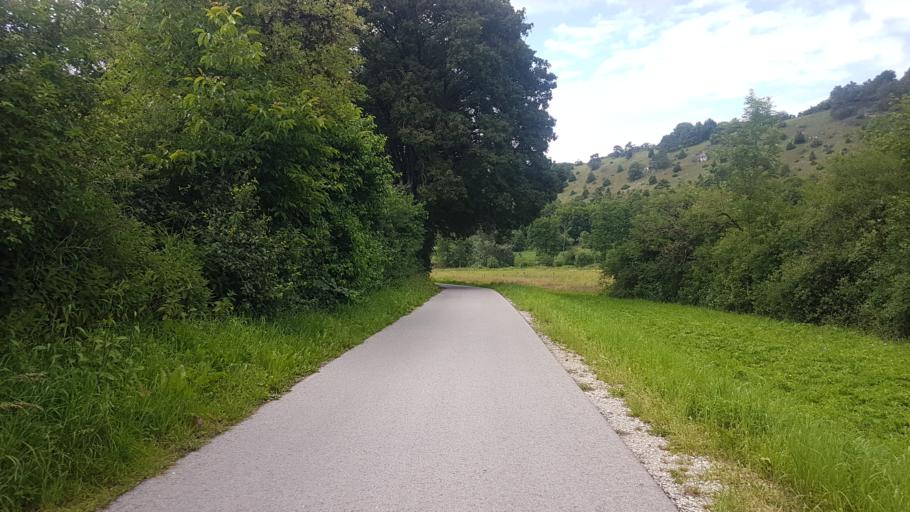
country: DE
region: Bavaria
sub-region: Regierungsbezirk Mittelfranken
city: Solnhofen
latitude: 48.8928
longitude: 11.0108
